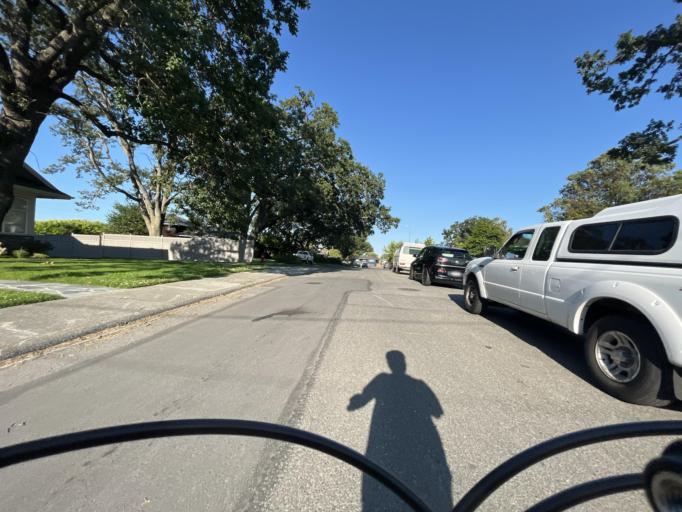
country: CA
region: British Columbia
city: Oak Bay
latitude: 48.4376
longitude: -123.3192
